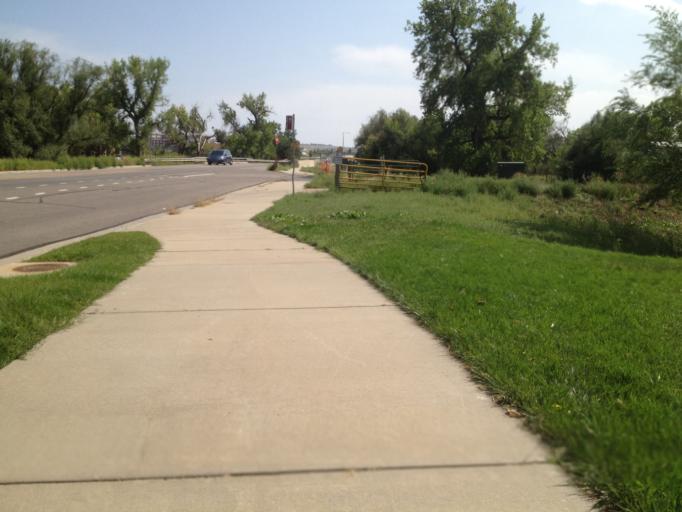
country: US
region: Colorado
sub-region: Boulder County
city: Lafayette
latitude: 39.9806
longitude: -105.0907
